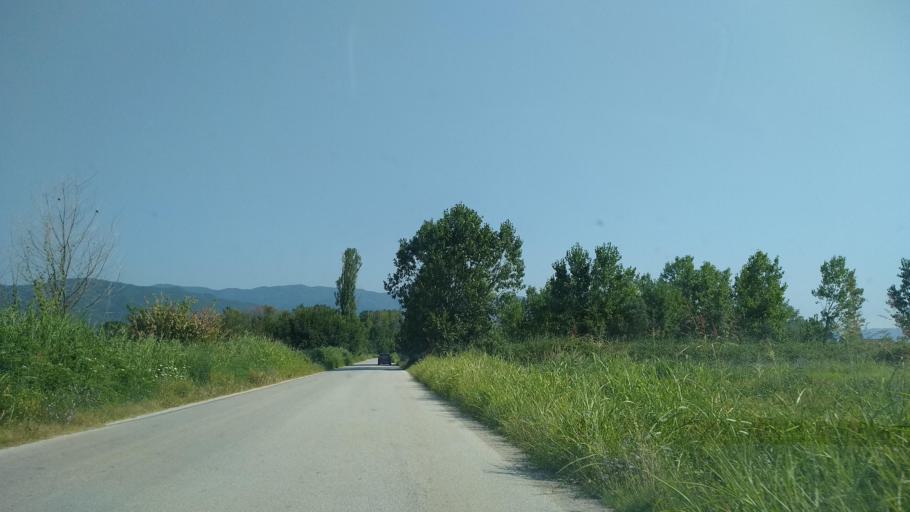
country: GR
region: Central Macedonia
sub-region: Nomos Thessalonikis
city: Stavros
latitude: 40.6774
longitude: 23.6876
